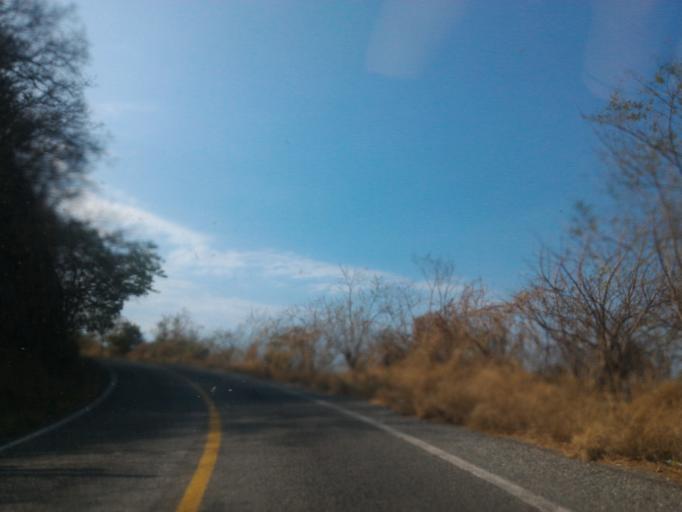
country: MX
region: Michoacan
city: Coahuayana Viejo
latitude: 18.4937
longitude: -103.5729
